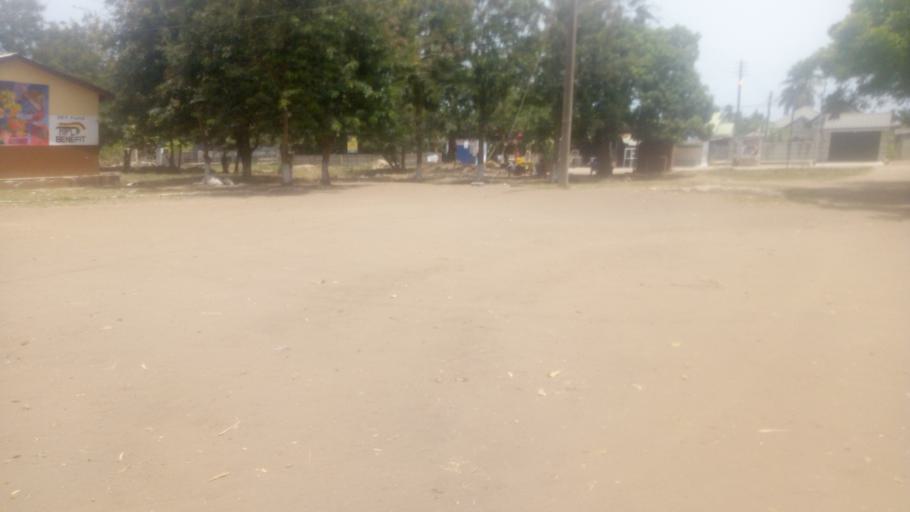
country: GH
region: Central
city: Winneba
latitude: 5.3592
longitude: -0.6317
